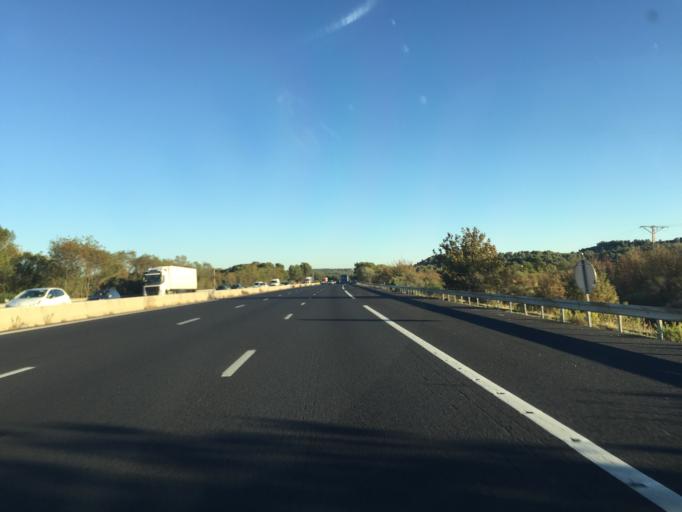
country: FR
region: Provence-Alpes-Cote d'Azur
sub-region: Departement des Bouches-du-Rhone
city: Lancon-Provence
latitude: 43.6112
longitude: 5.1456
